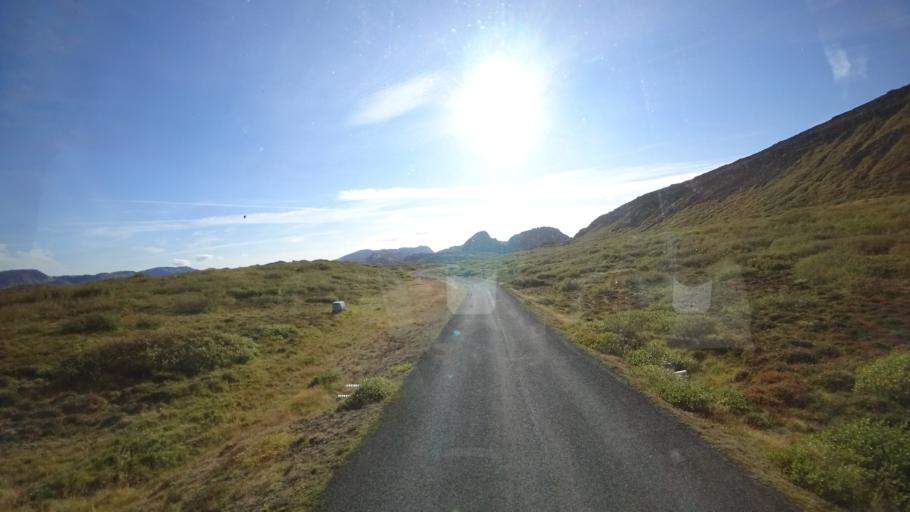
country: IS
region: South
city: Hveragerdi
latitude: 64.1619
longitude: -21.2458
